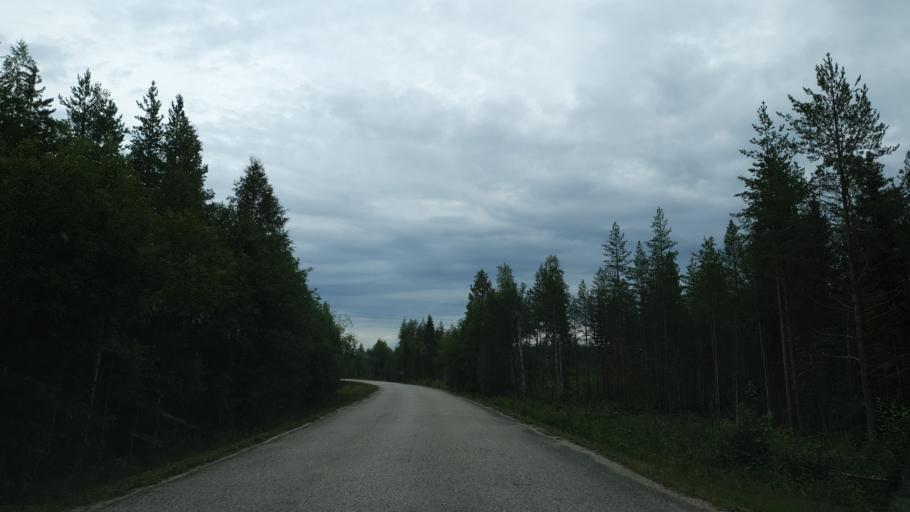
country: FI
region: Kainuu
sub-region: Kehys-Kainuu
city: Kuhmo
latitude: 64.3503
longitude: 29.1338
